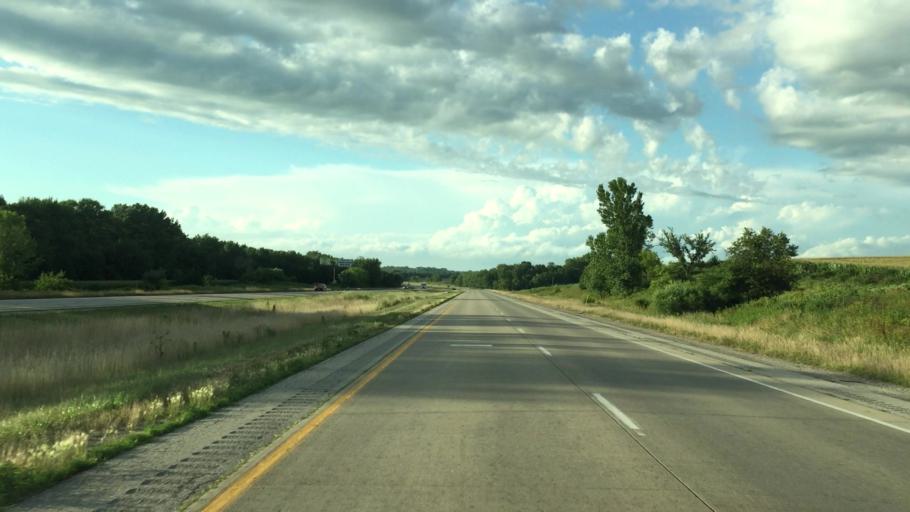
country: US
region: Iowa
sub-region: Johnson County
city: Lone Tree
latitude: 41.4550
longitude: -91.5498
